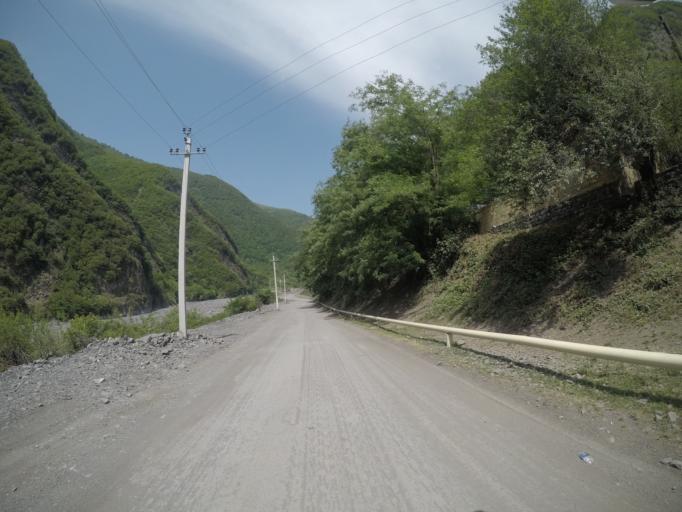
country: AZ
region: Qakh Rayon
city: Qaxbas
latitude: 41.4620
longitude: 47.0309
